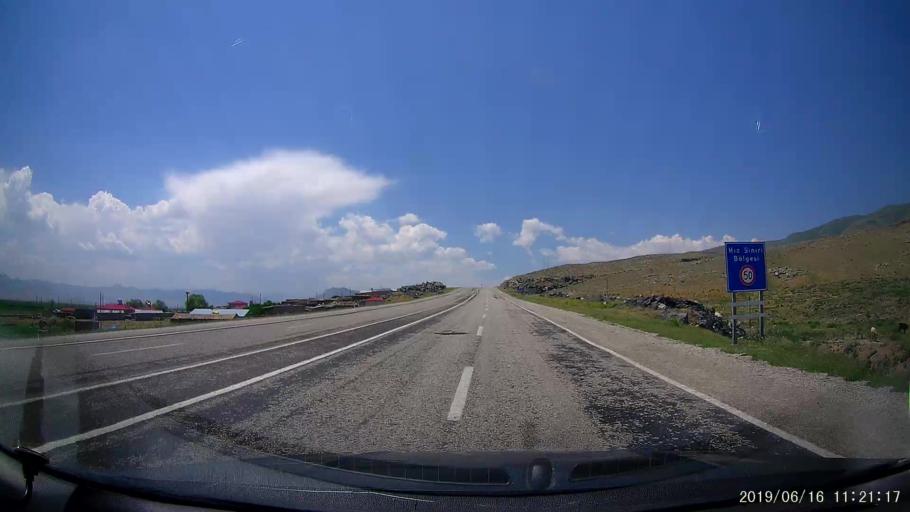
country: TR
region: Agri
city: Dogubayazit
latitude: 39.6936
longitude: 44.0736
